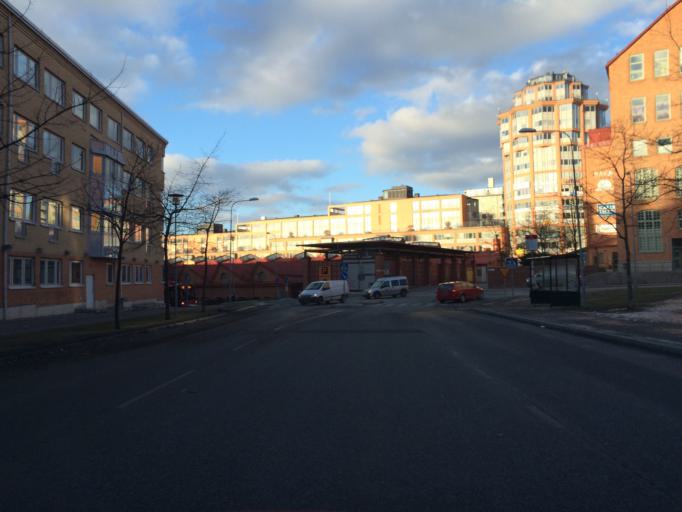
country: SE
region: Stockholm
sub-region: Nacka Kommun
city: Nacka
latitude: 59.3144
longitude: 18.1627
